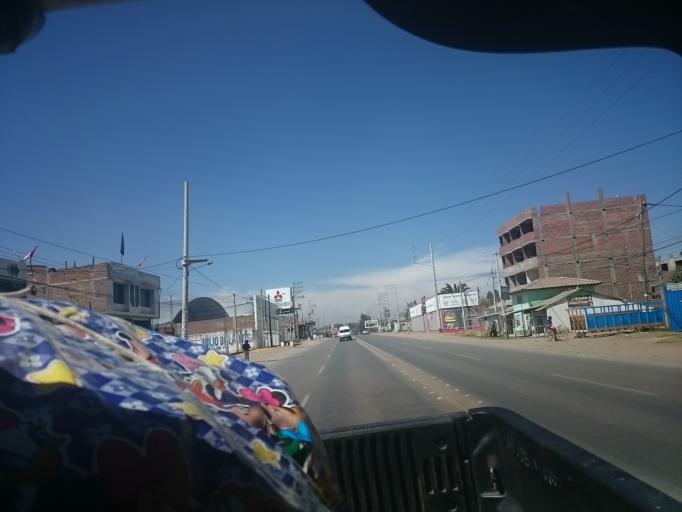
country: PE
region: Junin
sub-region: Provincia de Huancayo
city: Pilcomay
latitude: -12.0147
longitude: -75.2443
